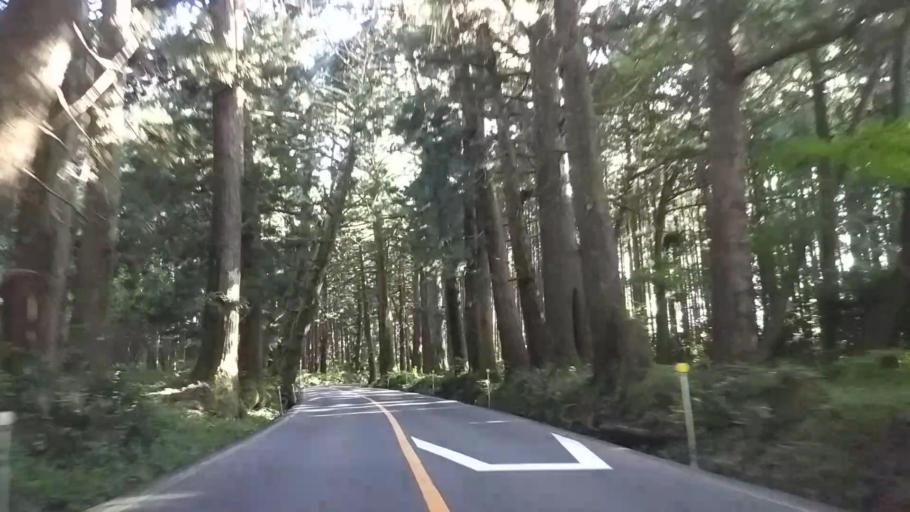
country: JP
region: Tochigi
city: Imaichi
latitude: 36.7586
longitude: 139.7095
